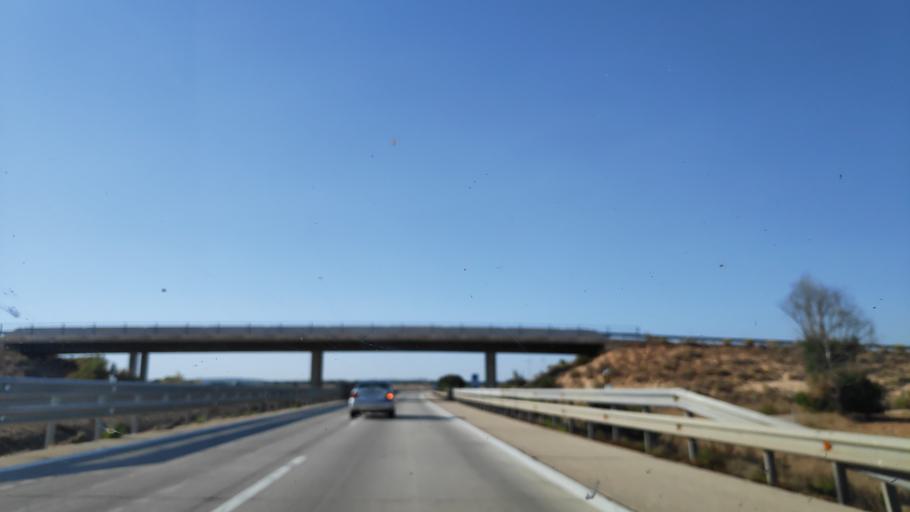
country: ES
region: Castille-La Mancha
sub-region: Provincia de Cuenca
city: Casas de Guijarro
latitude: 39.3145
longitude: -2.2035
